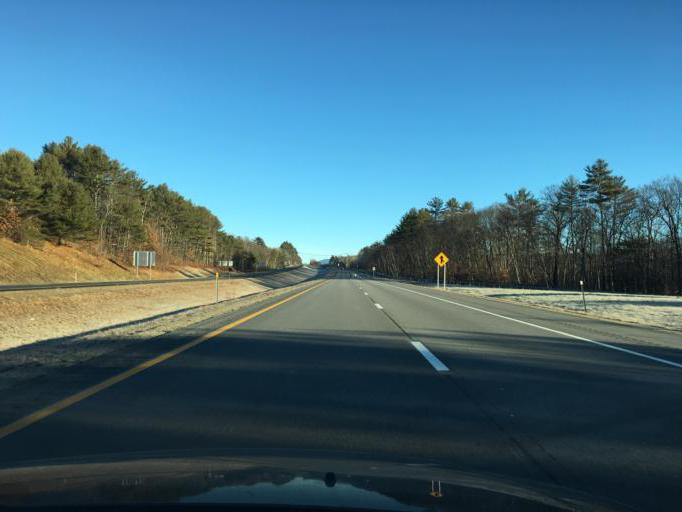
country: US
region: New Hampshire
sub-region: Grafton County
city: Plymouth
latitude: 43.7744
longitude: -71.6814
